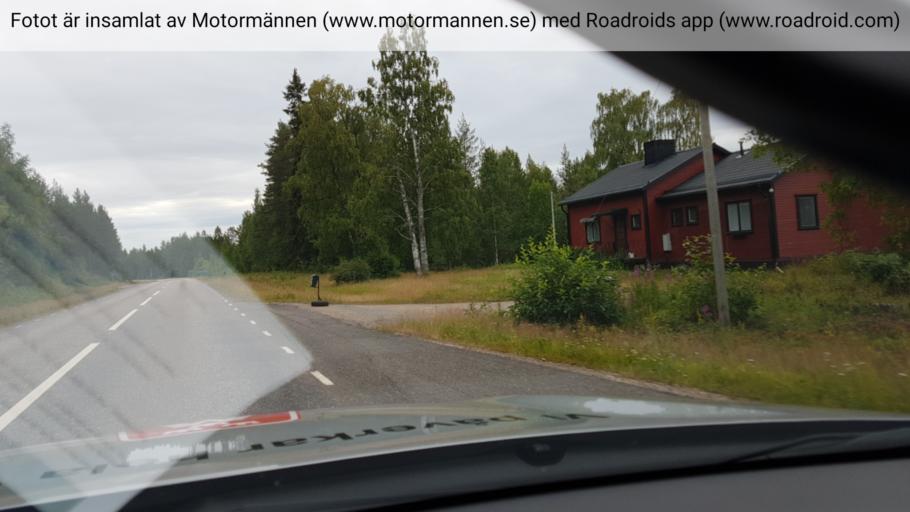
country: SE
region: Norrbotten
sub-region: Overkalix Kommun
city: OEverkalix
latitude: 66.4771
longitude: 22.7882
